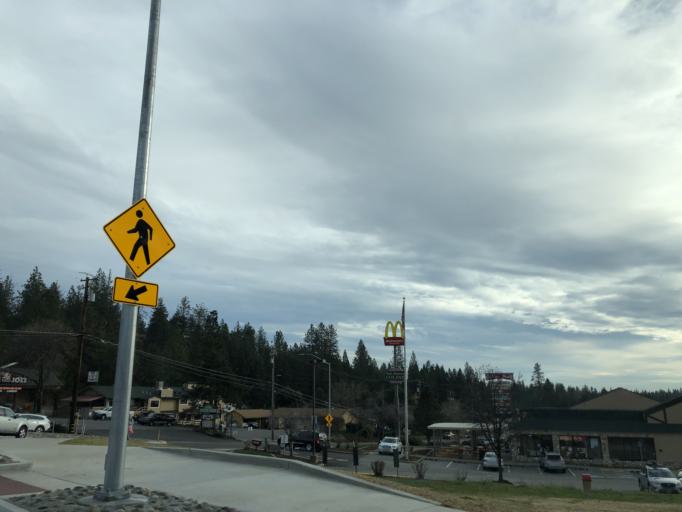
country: US
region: California
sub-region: Placer County
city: Colfax
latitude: 39.0948
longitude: -120.9512
